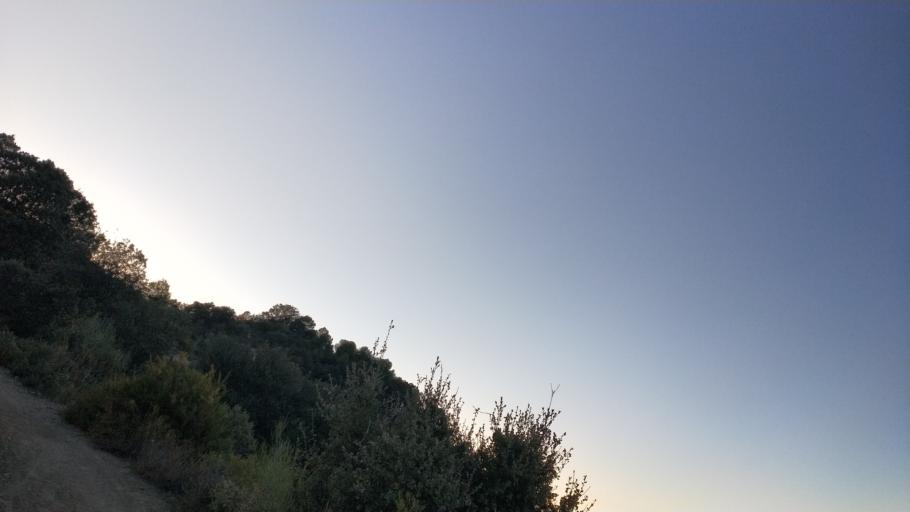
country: ES
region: Andalusia
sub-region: Provincia de Granada
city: Huetor Santillan
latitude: 37.2047
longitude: -3.5005
